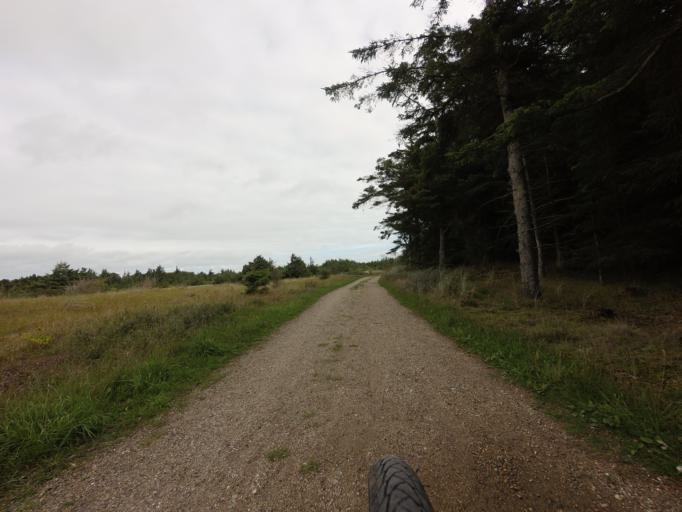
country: DK
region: North Denmark
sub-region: Hjorring Kommune
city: Hirtshals
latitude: 57.5533
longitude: 9.9225
